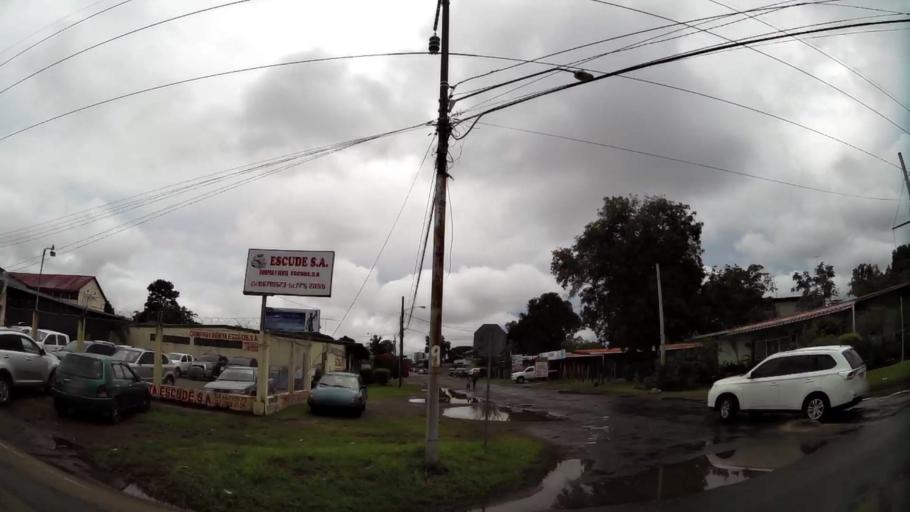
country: PA
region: Chiriqui
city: David
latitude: 8.4304
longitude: -82.4325
